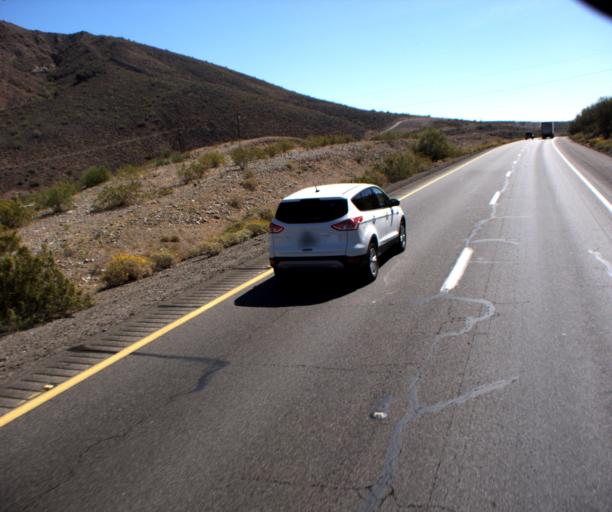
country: US
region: Arizona
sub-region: La Paz County
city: Quartzsite
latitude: 33.6752
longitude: -114.0526
